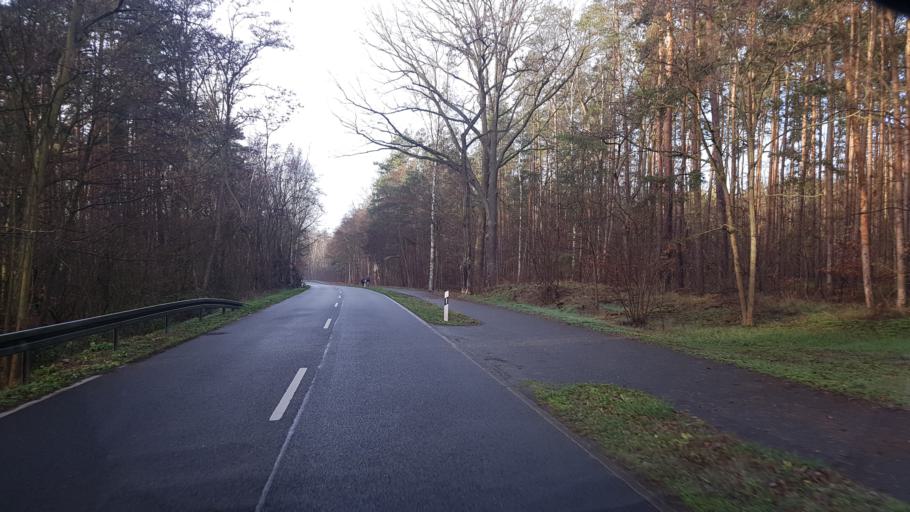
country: DE
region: Brandenburg
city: Doberlug-Kirchhain
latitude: 51.6315
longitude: 13.5318
